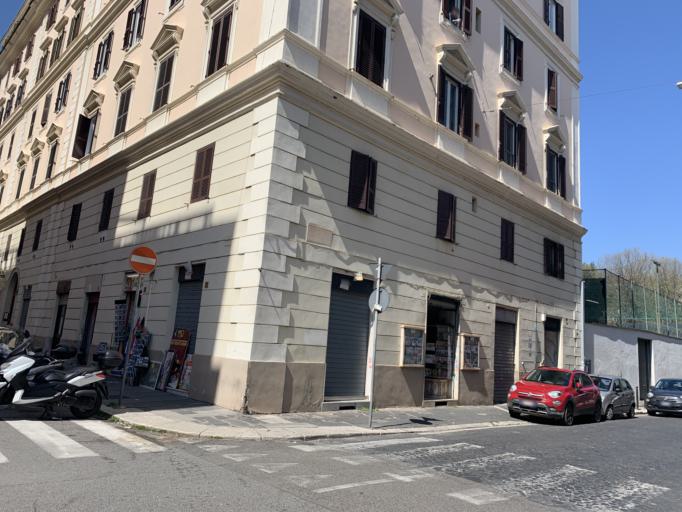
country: IT
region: Latium
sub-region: Citta metropolitana di Roma Capitale
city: Rome
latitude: 41.9069
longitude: 12.5019
